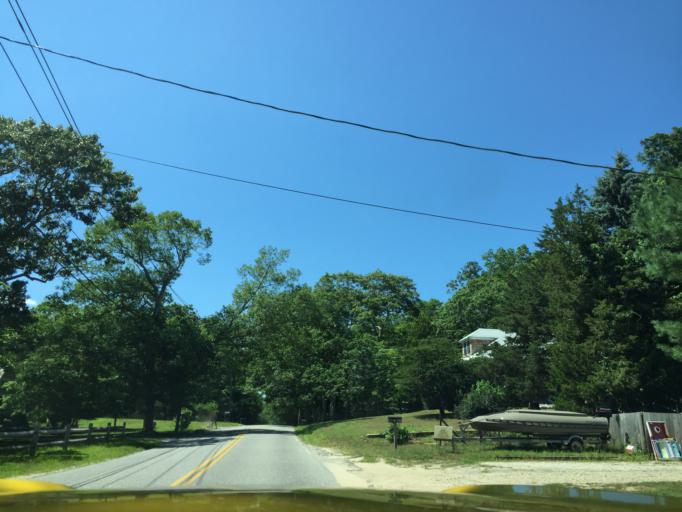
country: US
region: New York
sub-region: Suffolk County
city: Springs
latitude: 41.0037
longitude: -72.1340
